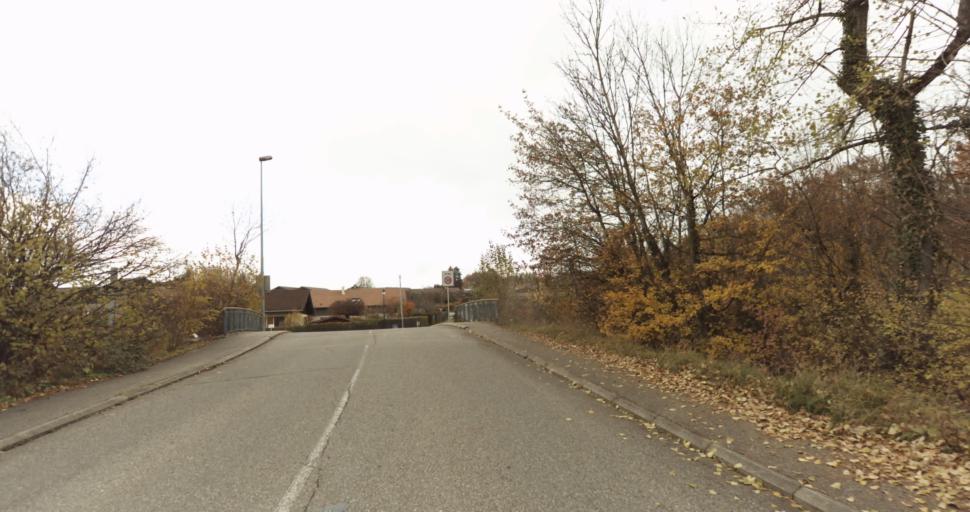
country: FR
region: Rhone-Alpes
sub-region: Departement de la Haute-Savoie
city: Pringy
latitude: 45.9448
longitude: 6.1283
